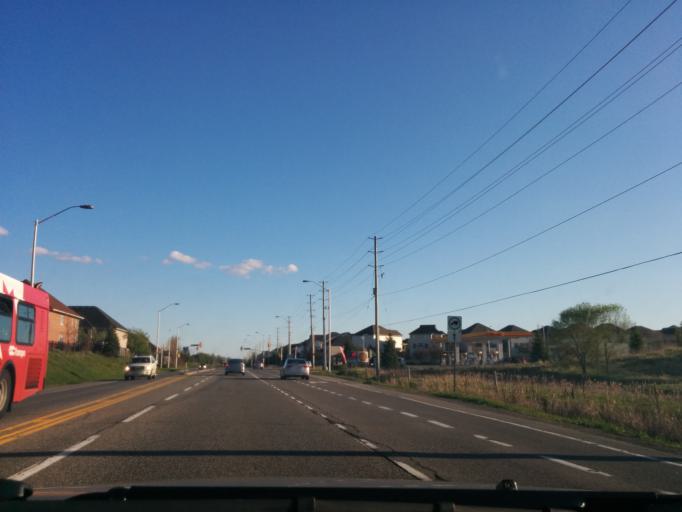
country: CA
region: Ontario
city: Ottawa
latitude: 45.2881
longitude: -75.7021
